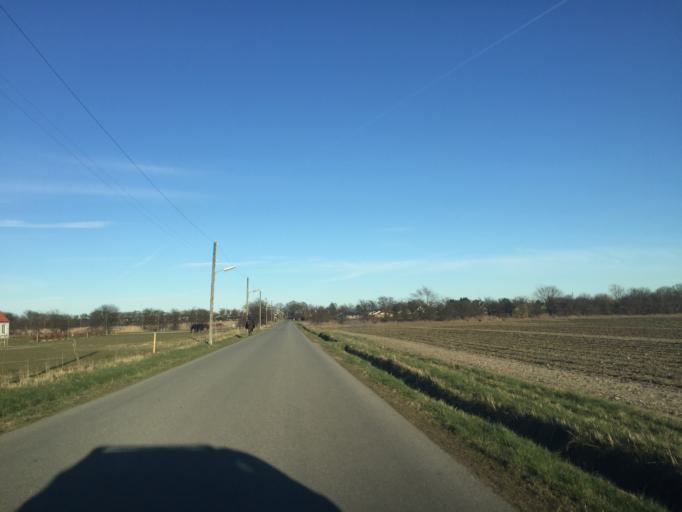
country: DK
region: Capital Region
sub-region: Dragor Kommune
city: Dragor
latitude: 55.6014
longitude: 12.6483
